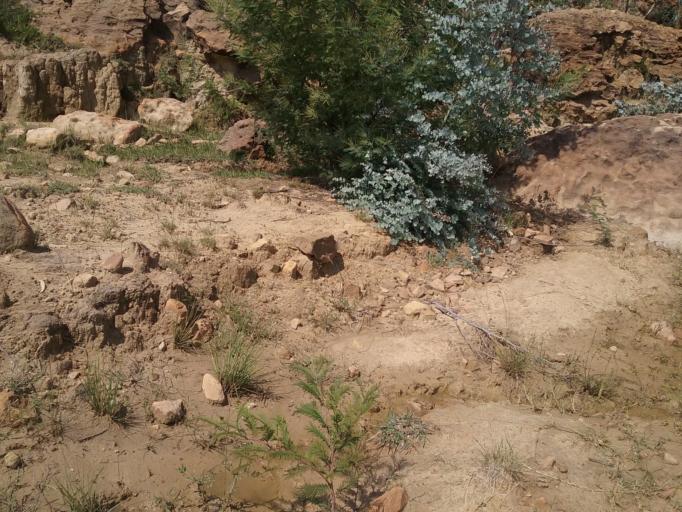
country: LS
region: Maseru
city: Maseru
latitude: -29.4251
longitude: 27.5760
